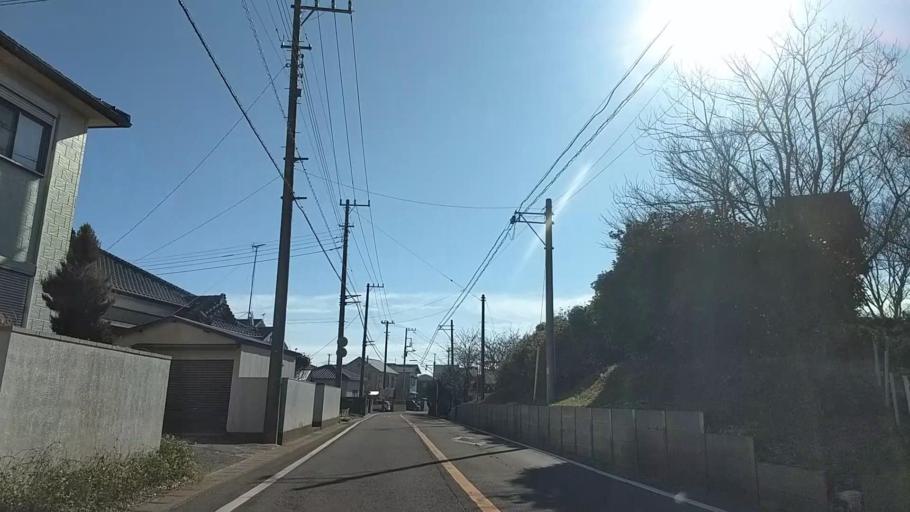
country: JP
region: Chiba
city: Hasaki
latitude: 35.7228
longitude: 140.8519
